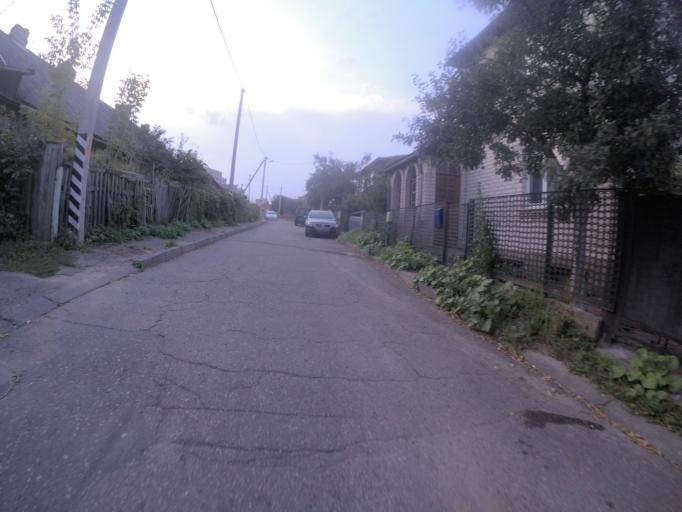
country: BY
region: Grodnenskaya
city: Hrodna
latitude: 53.6912
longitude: 23.8283
